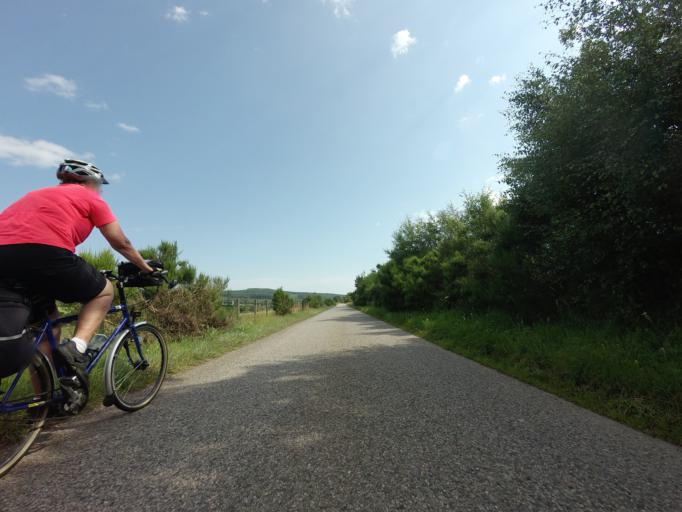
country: GB
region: Scotland
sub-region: Highland
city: Invergordon
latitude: 57.7473
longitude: -4.1677
